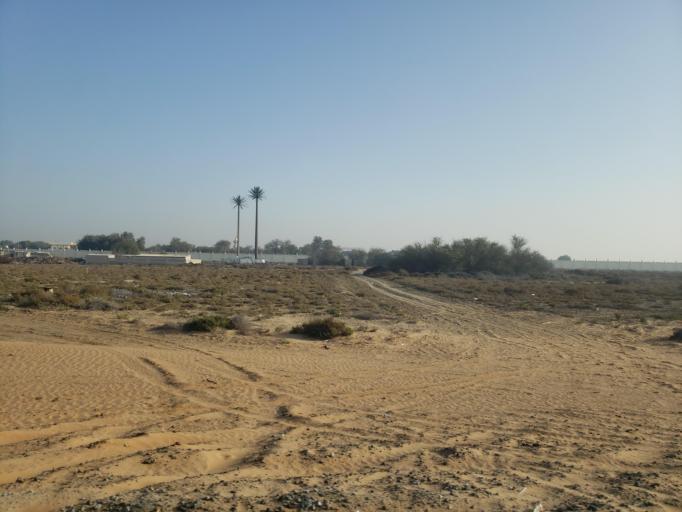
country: AE
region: Umm al Qaywayn
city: Umm al Qaywayn
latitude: 25.5223
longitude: 55.5613
